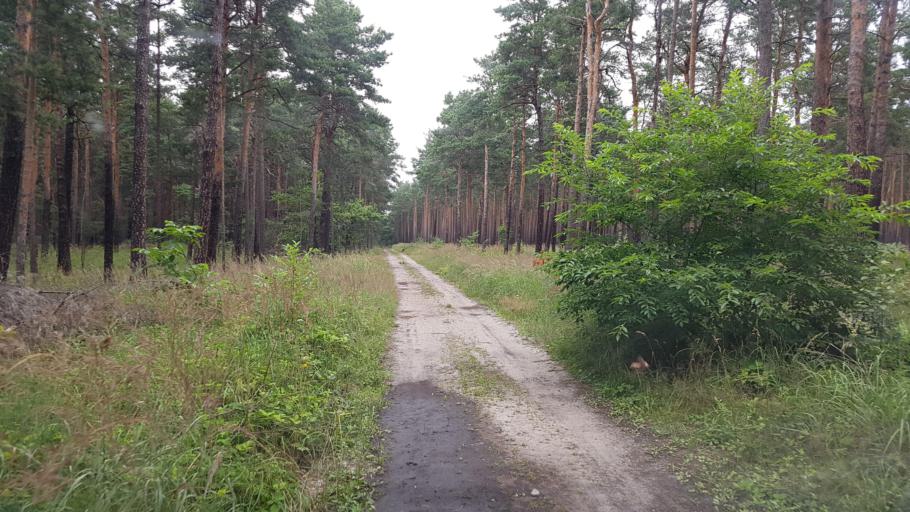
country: DE
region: Brandenburg
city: Grossraschen
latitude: 51.5930
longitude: 14.0369
